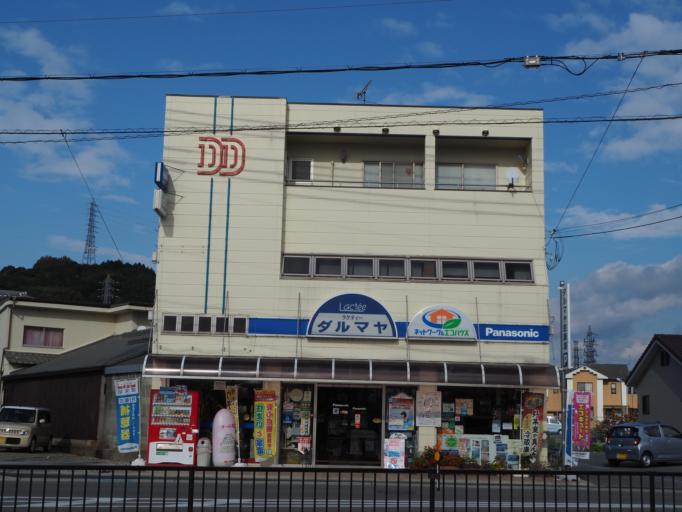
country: JP
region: Hyogo
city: Himeji
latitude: 34.9283
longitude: 134.7424
